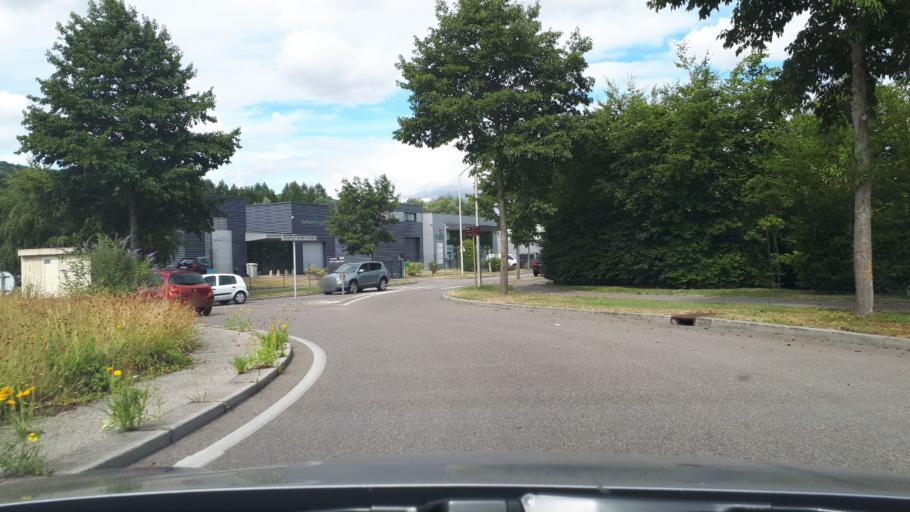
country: FR
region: Rhone-Alpes
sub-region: Departement de l'Isere
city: Domarin
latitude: 45.5886
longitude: 5.2548
